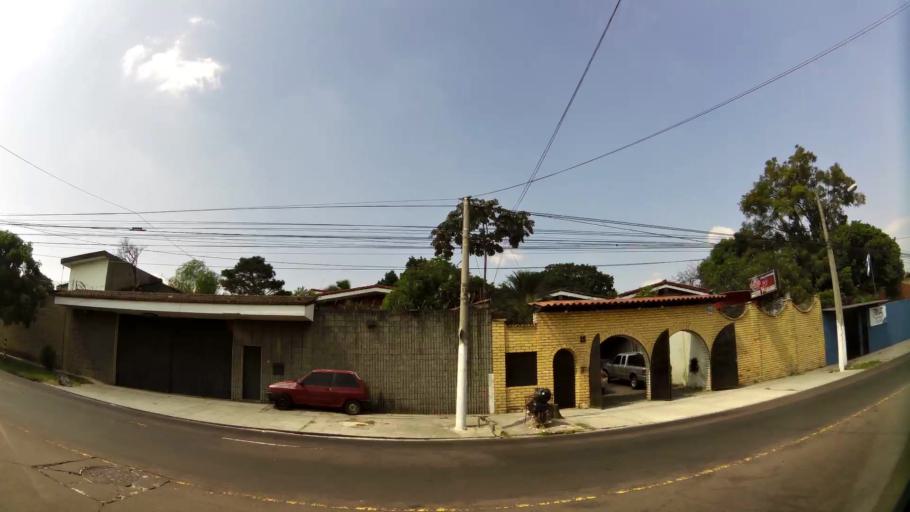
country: SV
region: San Salvador
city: San Salvador
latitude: 13.6902
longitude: -89.2224
